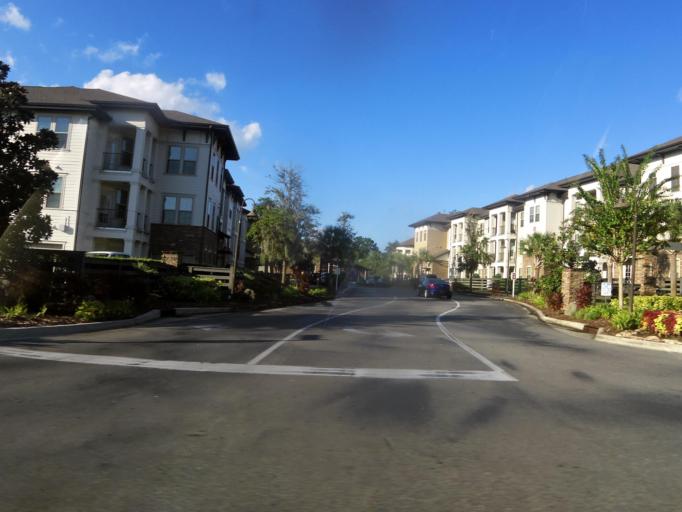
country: US
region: Florida
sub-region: Duval County
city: Jacksonville
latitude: 30.2472
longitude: -81.5590
